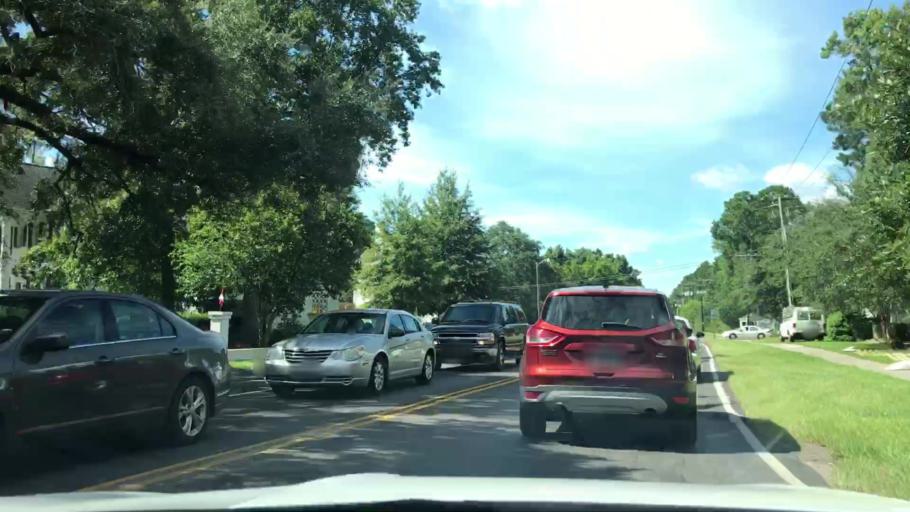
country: US
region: South Carolina
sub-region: Charleston County
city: North Charleston
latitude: 32.8214
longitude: -80.0364
